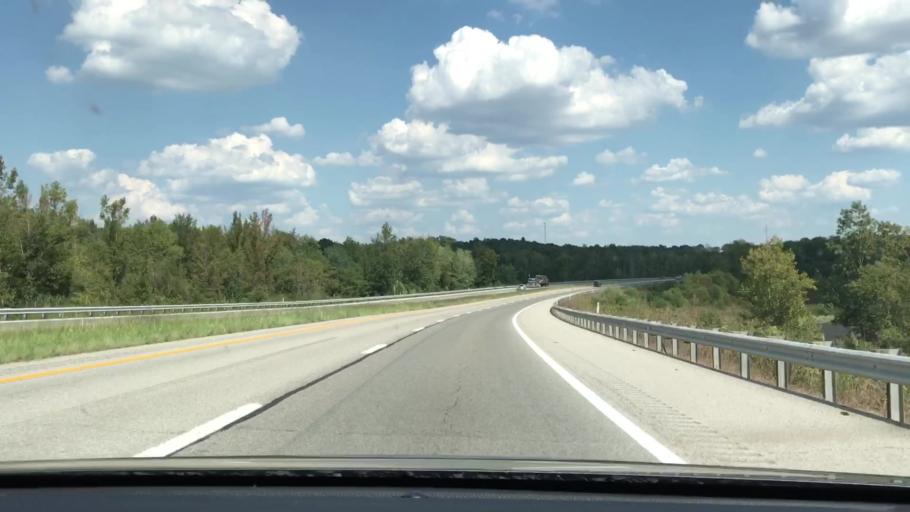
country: US
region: Kentucky
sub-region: Ohio County
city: Beaver Dam
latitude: 37.3306
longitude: -86.9848
